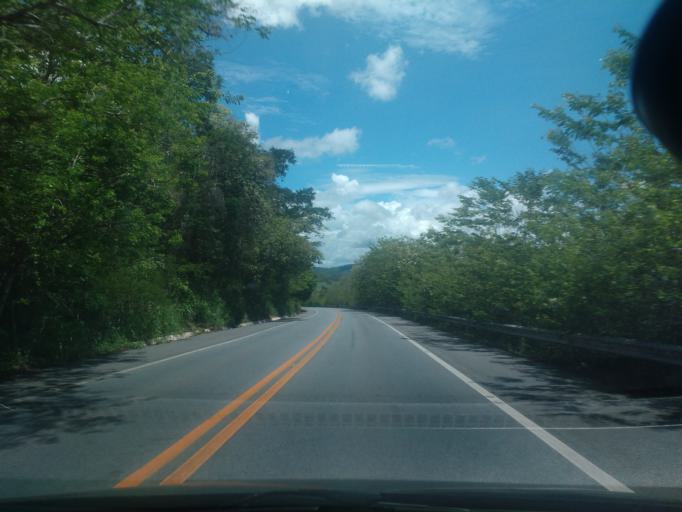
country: BR
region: Alagoas
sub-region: Uniao Dos Palmares
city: Uniao dos Palmares
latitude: -9.1384
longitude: -36.0187
